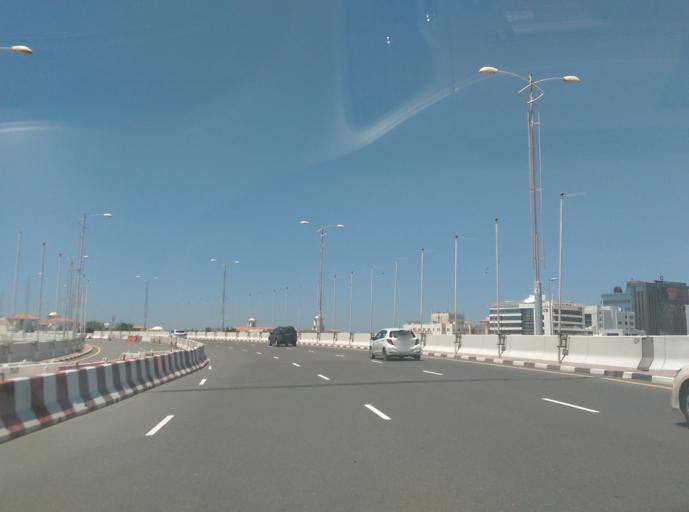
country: AE
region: Dubai
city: Dubai
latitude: 25.0988
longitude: 55.1624
